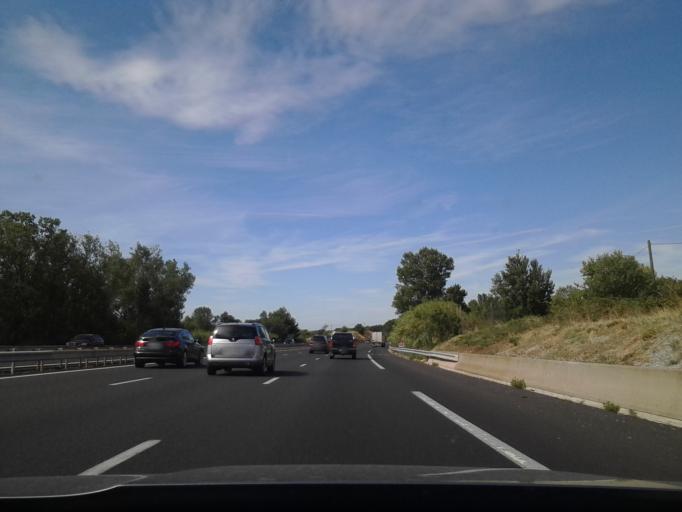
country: FR
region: Languedoc-Roussillon
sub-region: Departement de l'Herault
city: Meze
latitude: 43.4293
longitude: 3.5605
